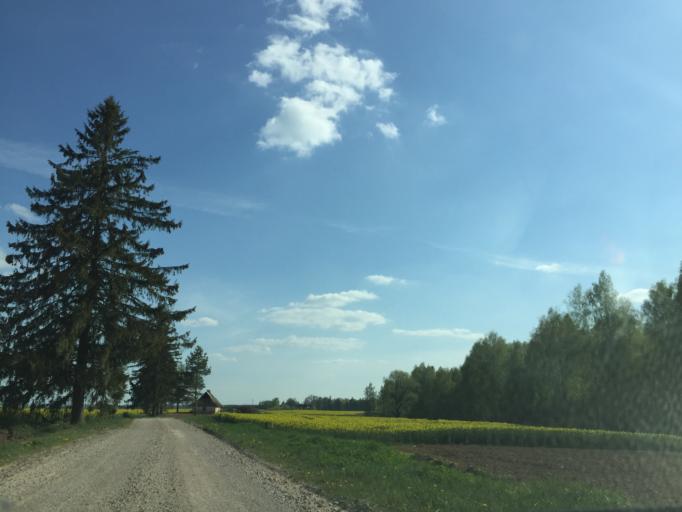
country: LV
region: Lecava
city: Iecava
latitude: 56.4999
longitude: 24.3183
